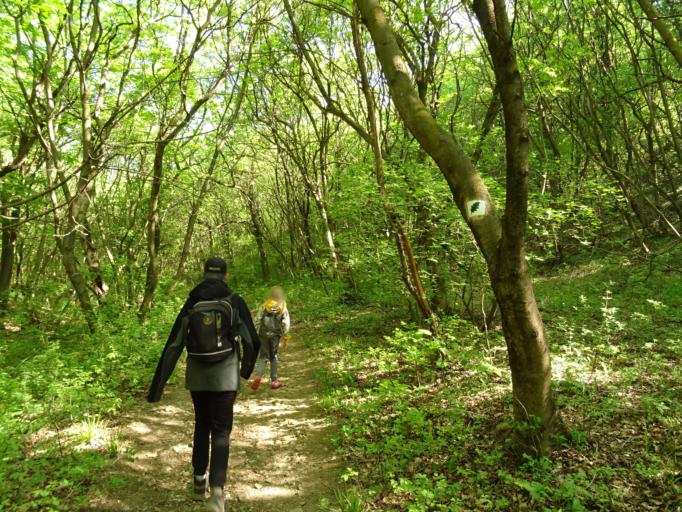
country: HU
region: Fejer
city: Csakvar
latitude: 47.3899
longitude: 18.4385
